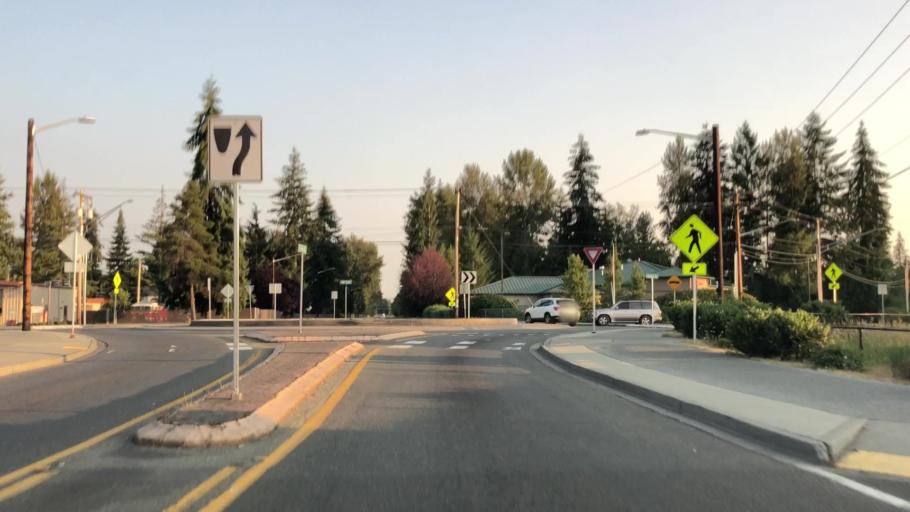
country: US
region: Washington
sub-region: Snohomish County
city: Marysville
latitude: 48.0931
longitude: -122.1624
